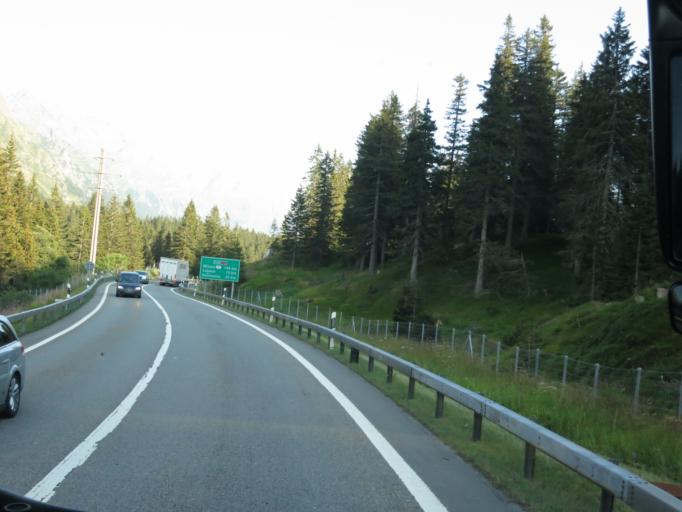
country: CH
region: Grisons
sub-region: Hinterrhein District
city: Hinterrhein
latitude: 46.4594
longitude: 9.1894
